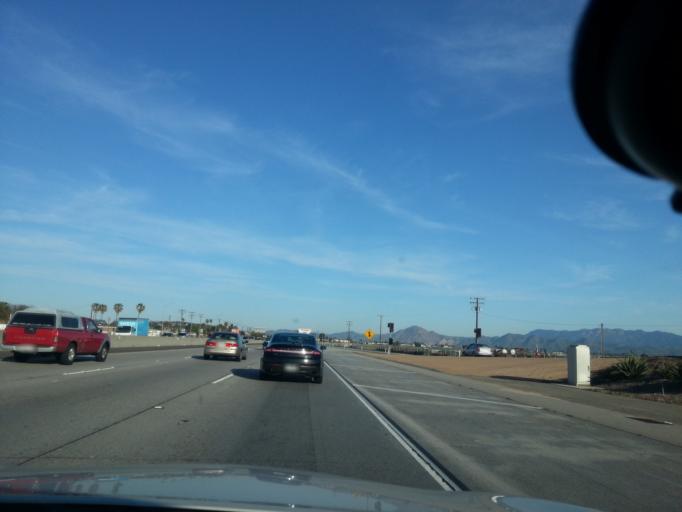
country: US
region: California
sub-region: Ventura County
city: El Rio
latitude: 34.2224
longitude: -119.1409
